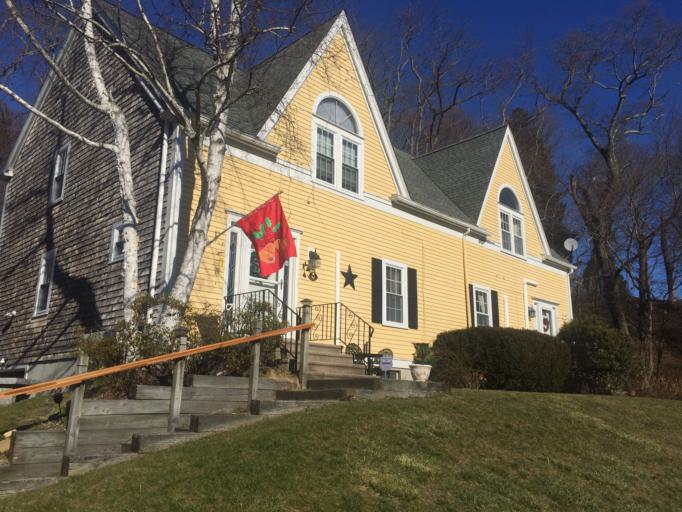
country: US
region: Massachusetts
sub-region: Plymouth County
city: Plymouth
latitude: 41.9589
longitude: -70.6746
